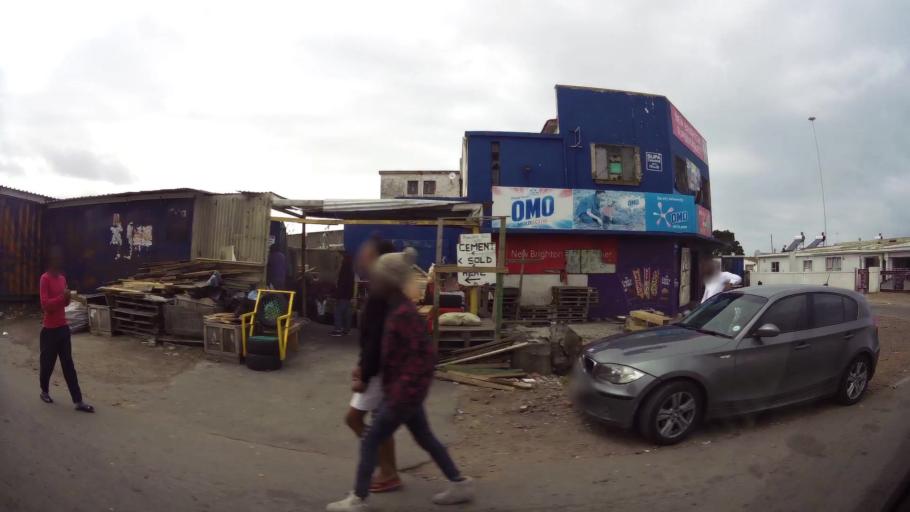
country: ZA
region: Eastern Cape
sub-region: Nelson Mandela Bay Metropolitan Municipality
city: Port Elizabeth
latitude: -33.8929
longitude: 25.6026
